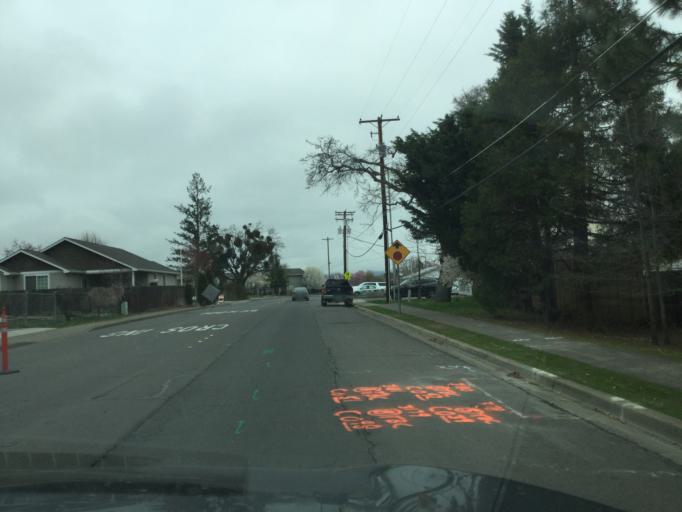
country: US
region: Oregon
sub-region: Jackson County
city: Central Point
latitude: 42.3850
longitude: -122.9197
